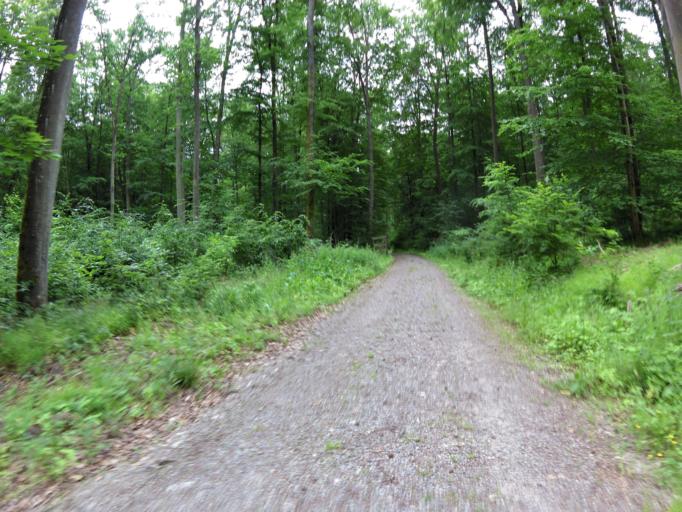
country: DE
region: Bavaria
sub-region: Regierungsbezirk Unterfranken
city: Margetshochheim
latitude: 49.8252
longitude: 9.8350
